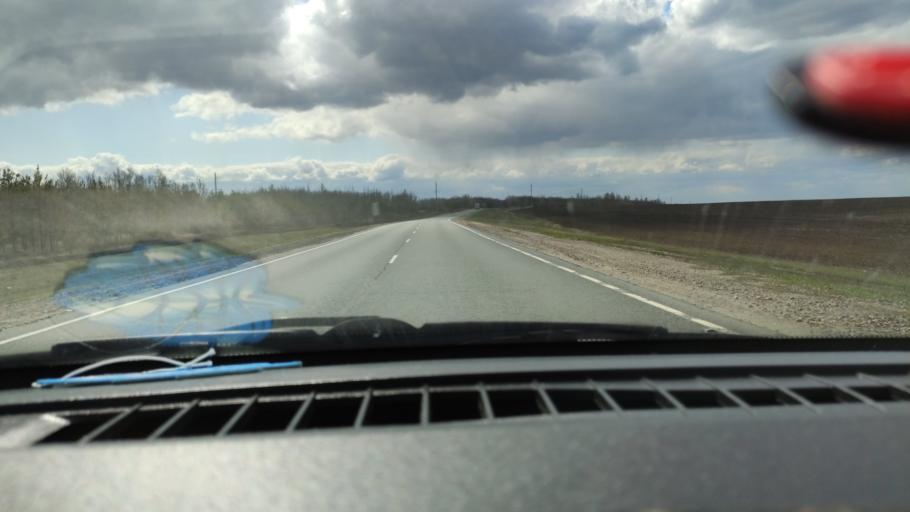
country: RU
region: Saratov
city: Alekseyevka
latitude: 52.2736
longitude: 47.9302
